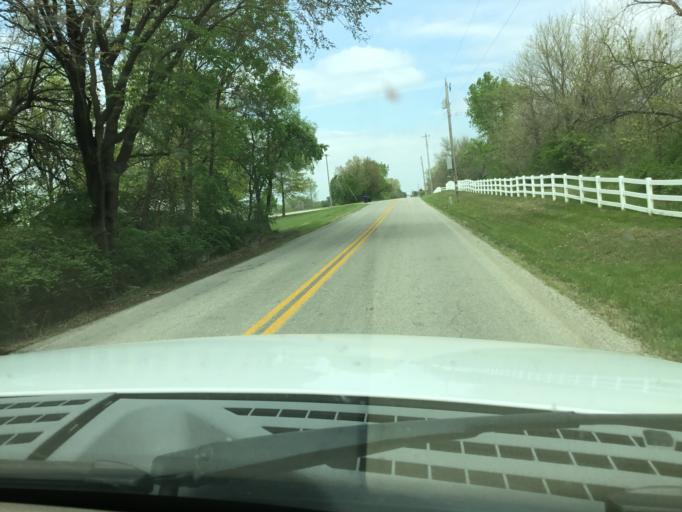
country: US
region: Kansas
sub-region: Shawnee County
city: Topeka
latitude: 38.9683
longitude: -95.6142
